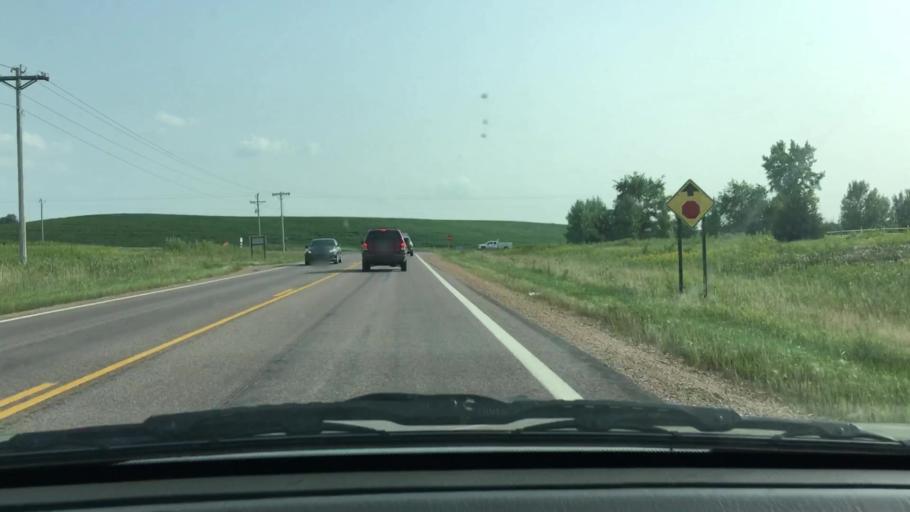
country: US
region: Minnesota
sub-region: Scott County
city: Elko New Market
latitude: 44.5453
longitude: -93.3396
